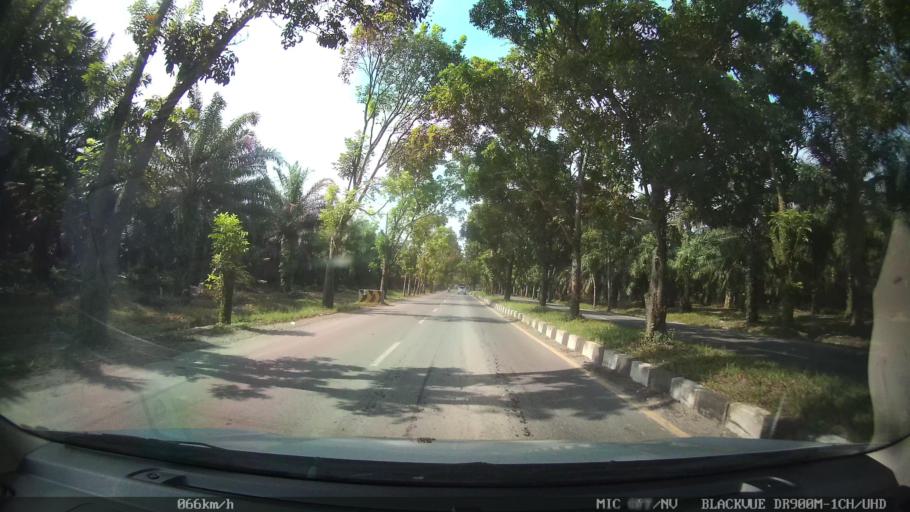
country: ID
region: North Sumatra
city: Binjai
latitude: 3.6392
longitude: 98.5353
